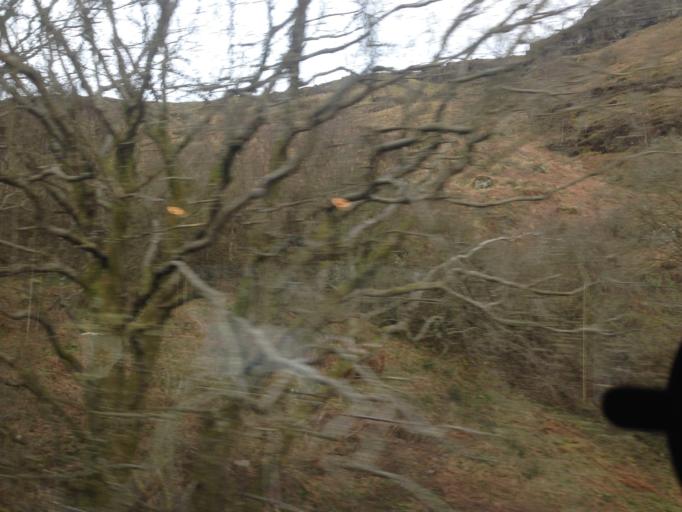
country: GB
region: Scotland
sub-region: Argyll and Bute
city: Garelochhead
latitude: 56.1757
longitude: -4.7745
